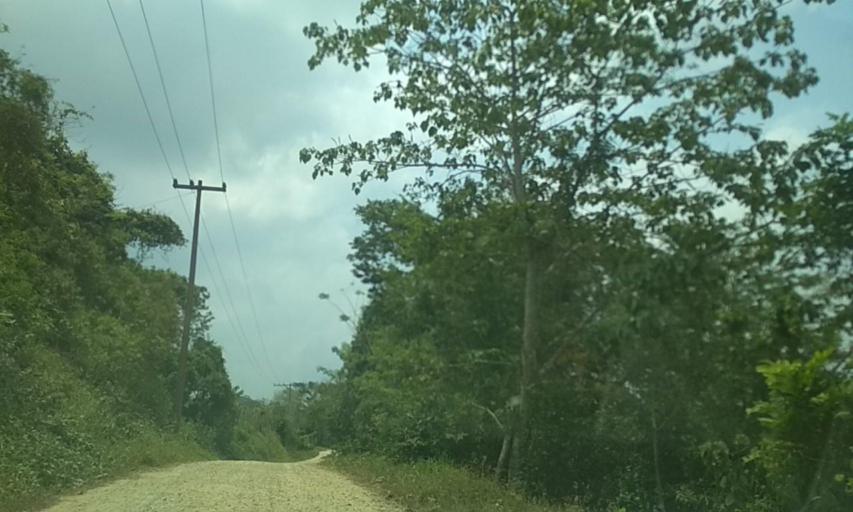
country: MX
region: Tabasco
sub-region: Huimanguillo
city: Francisco Rueda
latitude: 17.5947
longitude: -93.7943
